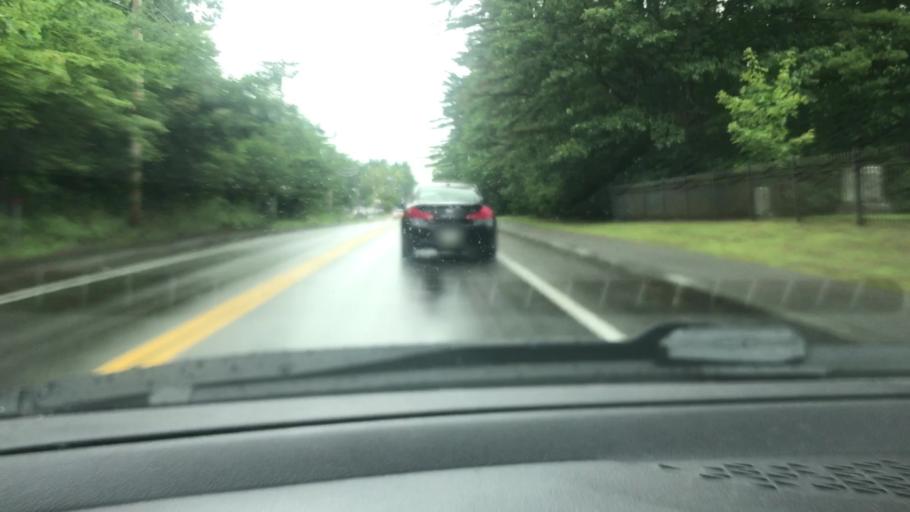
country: US
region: New Hampshire
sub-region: Merrimack County
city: East Concord
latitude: 43.2506
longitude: -71.5731
